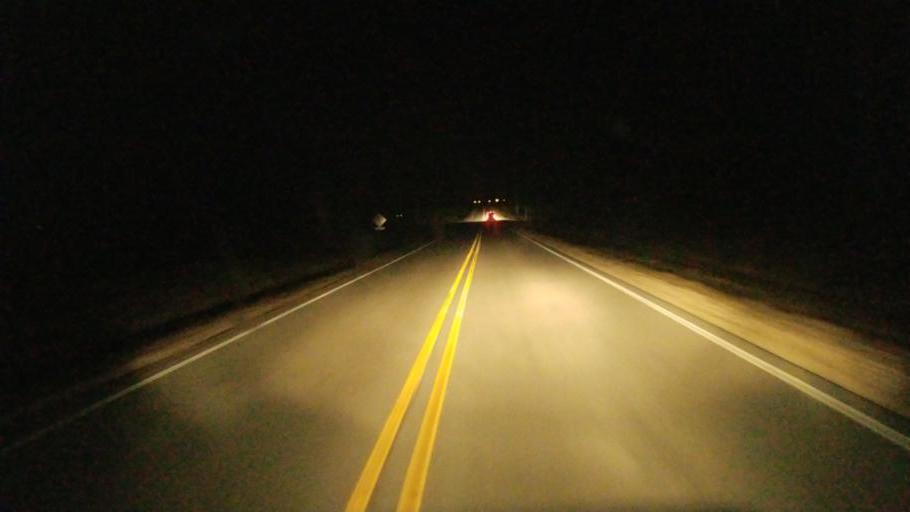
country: US
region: Illinois
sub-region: Henderson County
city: Oquawka
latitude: 40.7741
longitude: -90.8693
